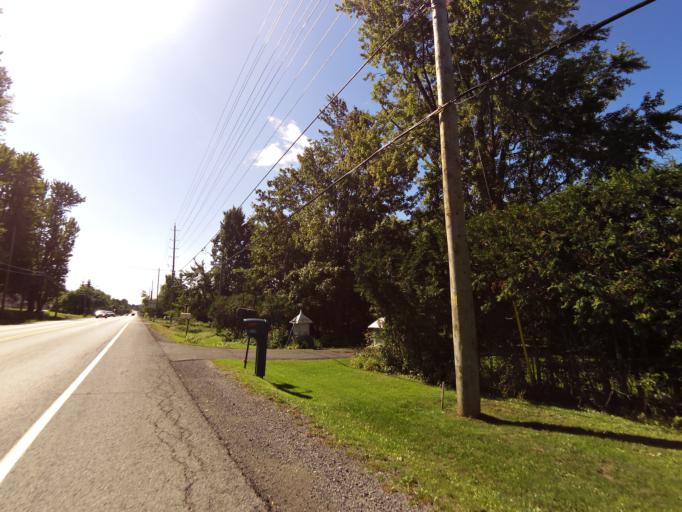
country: CA
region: Ontario
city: Bells Corners
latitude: 45.2684
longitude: -75.8304
